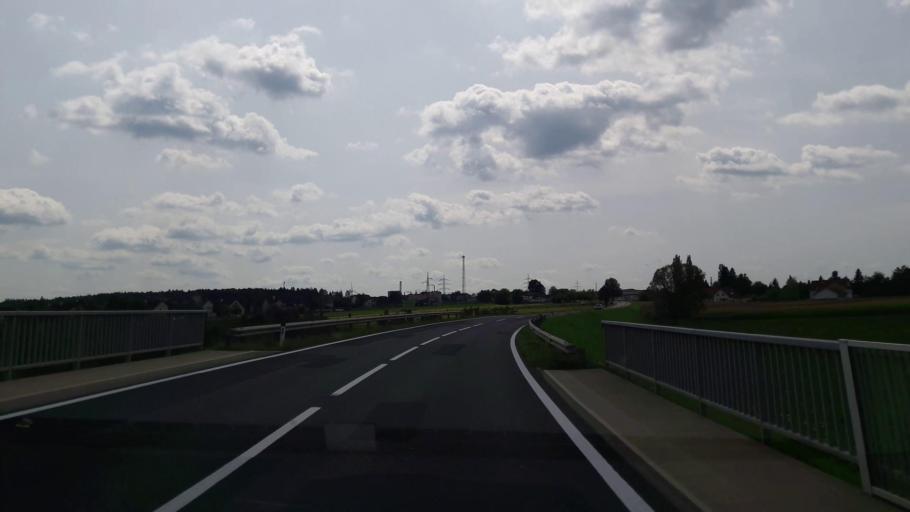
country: AT
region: Styria
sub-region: Politischer Bezirk Hartberg-Fuerstenfeld
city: Hartberg
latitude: 47.2696
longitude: 15.9712
